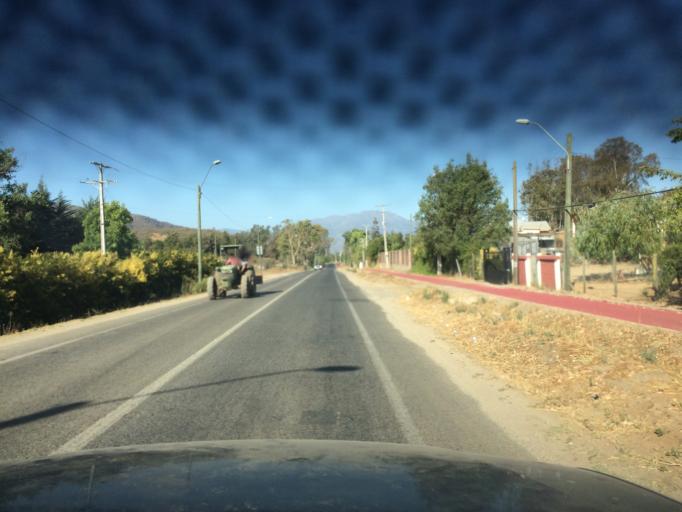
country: CL
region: Santiago Metropolitan
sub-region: Provincia de Melipilla
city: Melipilla
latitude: -33.4915
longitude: -71.1507
